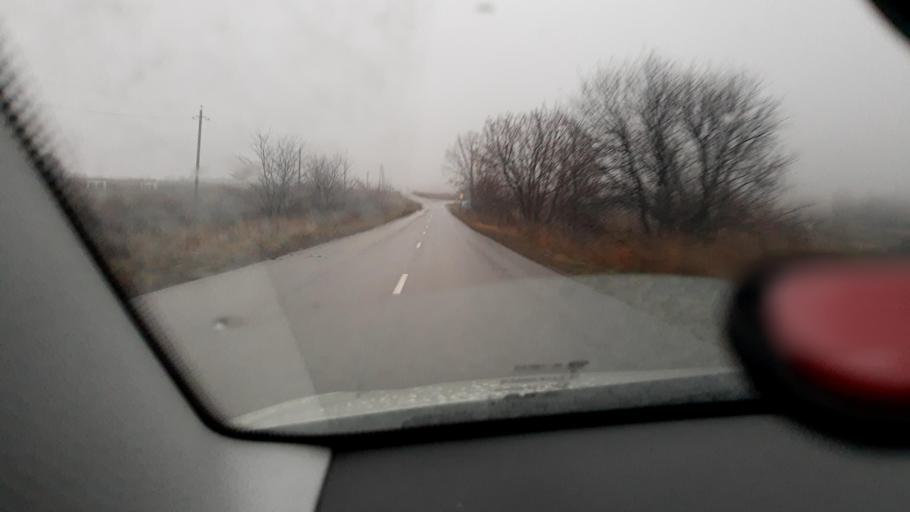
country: RU
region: Bashkortostan
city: Iglino
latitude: 54.9003
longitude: 56.2650
